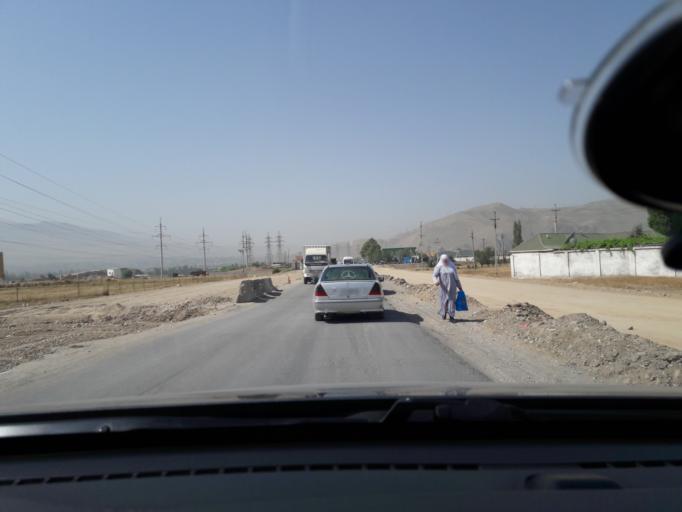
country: TJ
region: Dushanbe
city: Boshkengash
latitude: 38.4668
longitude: 68.7398
